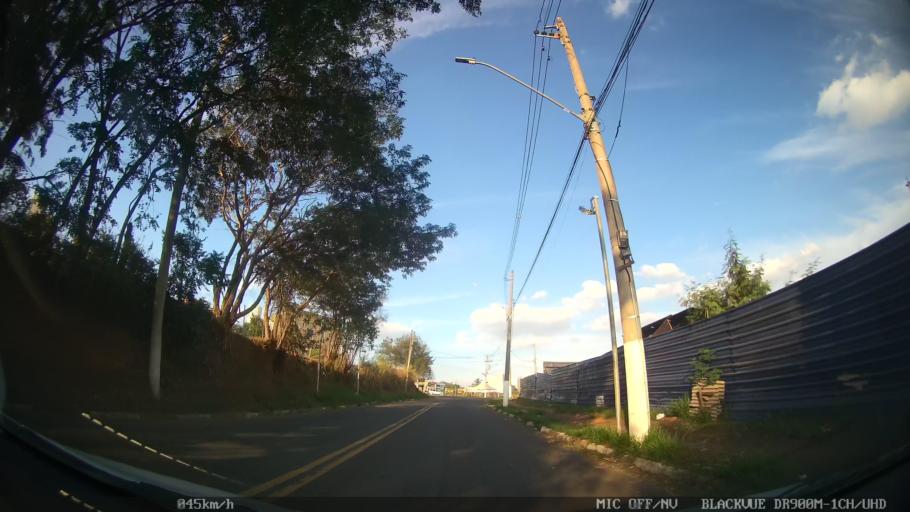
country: BR
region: Sao Paulo
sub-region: Hortolandia
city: Hortolandia
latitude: -22.8758
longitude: -47.1888
